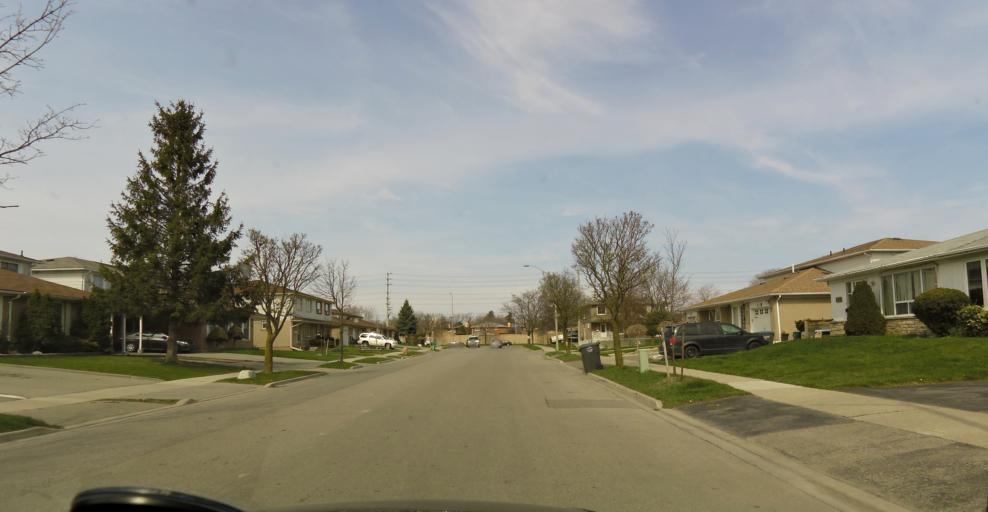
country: CA
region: Ontario
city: Mississauga
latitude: 43.5858
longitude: -79.5899
